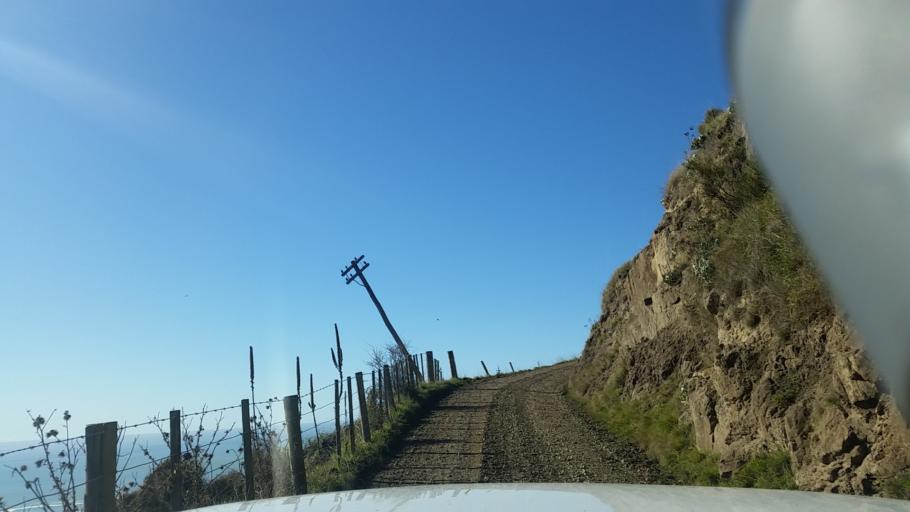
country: NZ
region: Canterbury
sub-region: Christchurch City
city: Christchurch
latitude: -43.6621
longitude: 172.9929
